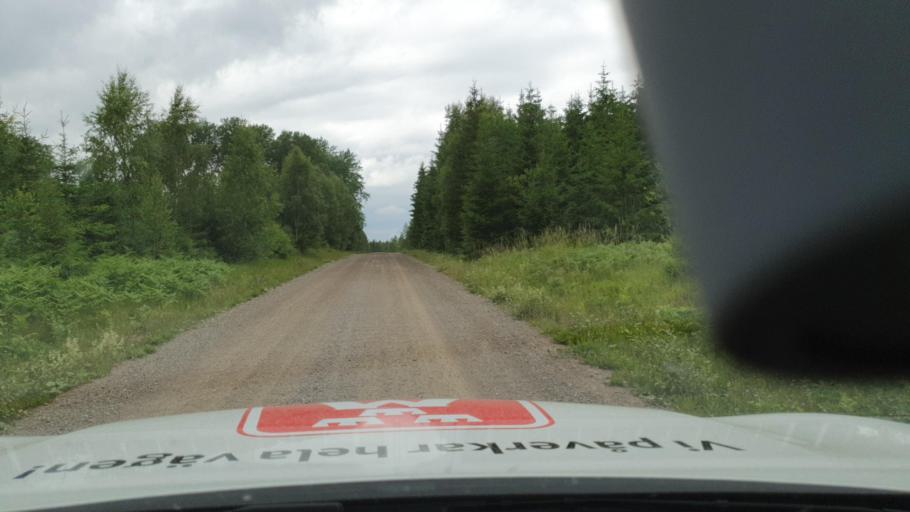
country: SE
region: Vaestra Goetaland
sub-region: Tidaholms Kommun
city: Tidaholm
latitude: 58.1601
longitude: 14.0544
